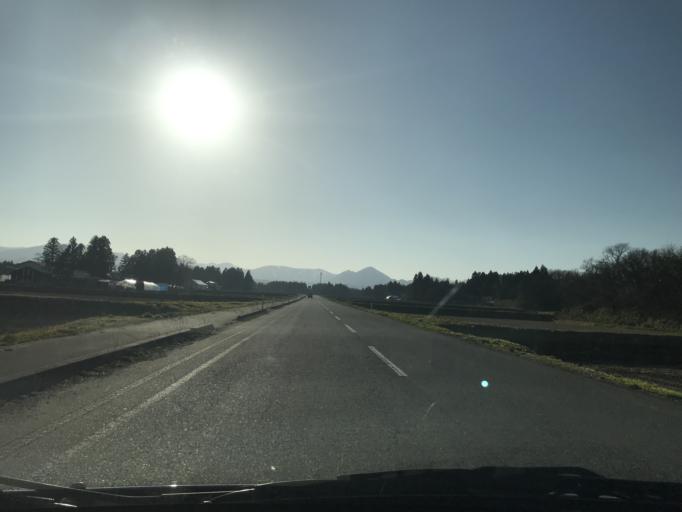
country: JP
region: Iwate
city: Kitakami
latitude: 39.2375
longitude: 141.0613
